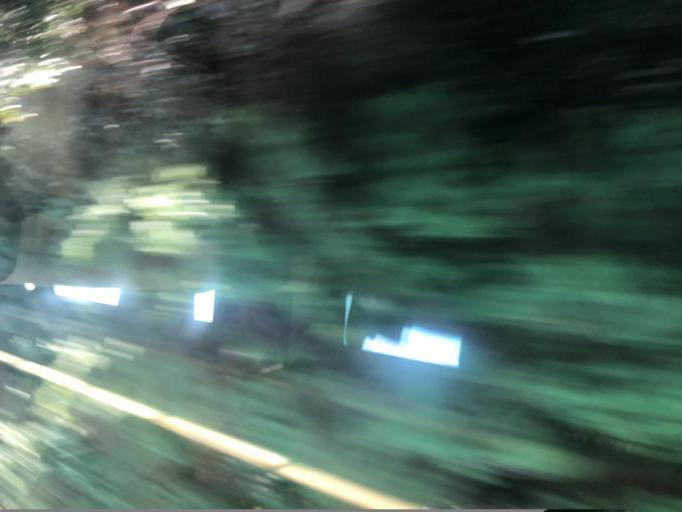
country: JP
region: Kochi
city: Nakamura
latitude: 33.0131
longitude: 132.9916
